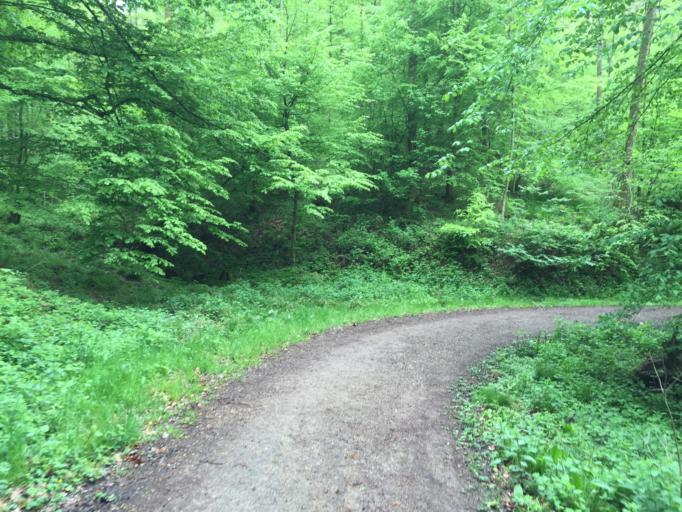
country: DE
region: Baden-Wuerttemberg
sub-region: Karlsruhe Region
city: Schriesheim
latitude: 49.5009
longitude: 8.6807
